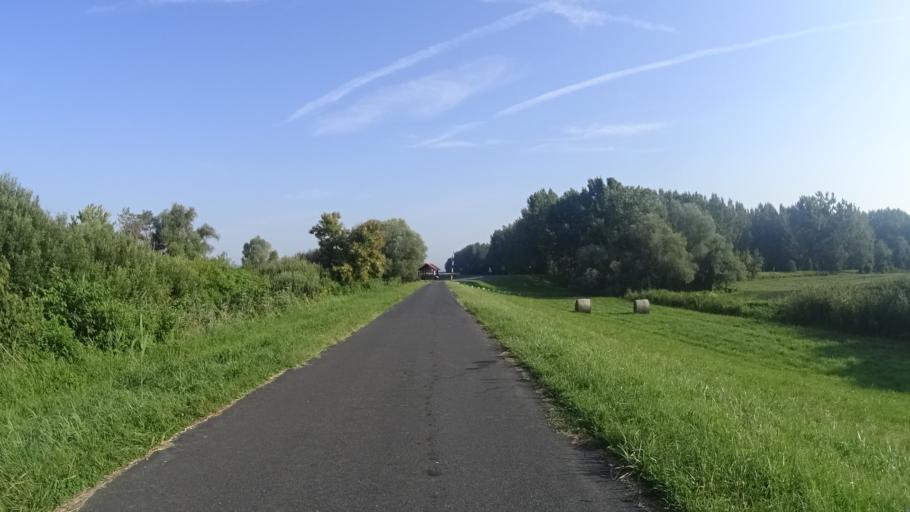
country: HU
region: Zala
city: Sarmellek
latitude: 46.6600
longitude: 17.1337
